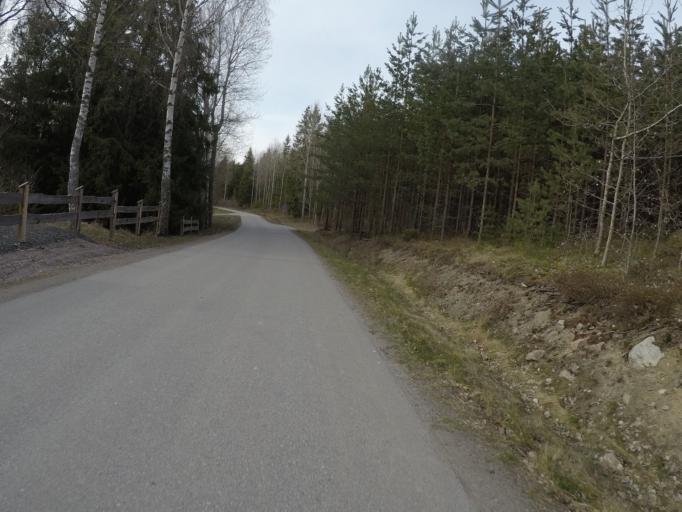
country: SE
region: Soedermanland
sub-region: Eskilstuna Kommun
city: Torshalla
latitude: 59.4414
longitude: 16.5139
